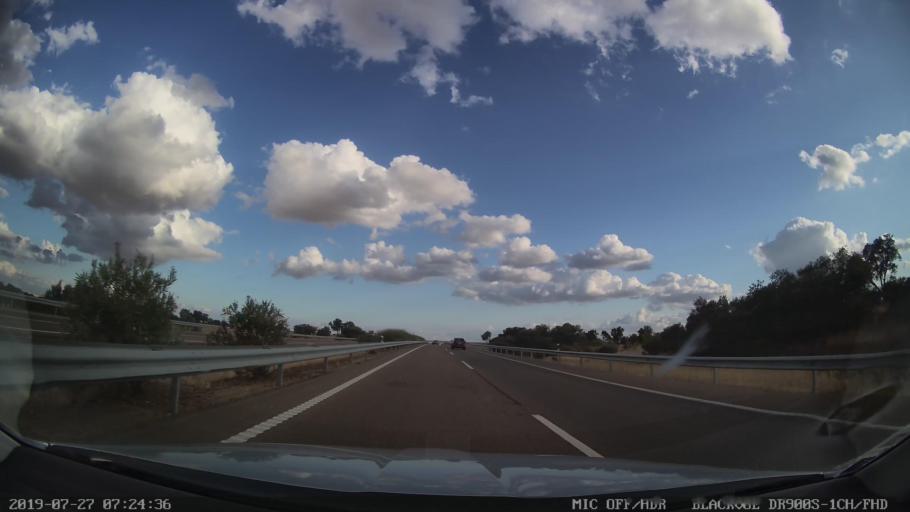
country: ES
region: Extremadura
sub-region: Provincia de Caceres
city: Puerto de Santa Cruz
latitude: 39.2941
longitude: -5.8554
